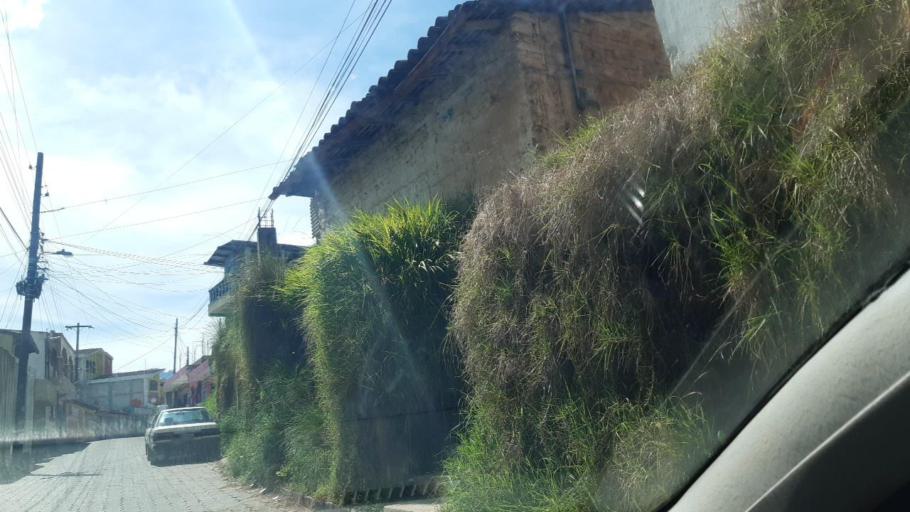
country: GT
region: Quetzaltenango
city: Salcaja
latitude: 14.8708
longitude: -91.4570
